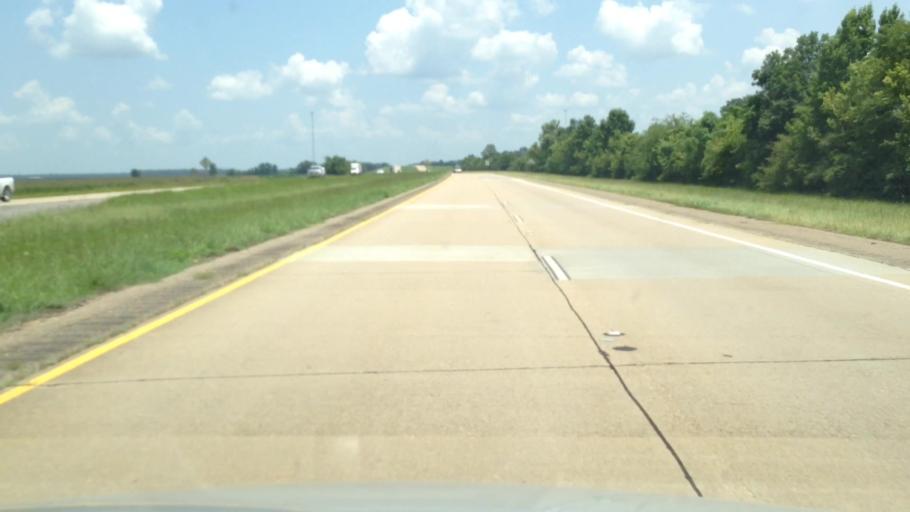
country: US
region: Louisiana
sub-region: Rapides Parish
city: Lecompte
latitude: 31.0195
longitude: -92.3883
